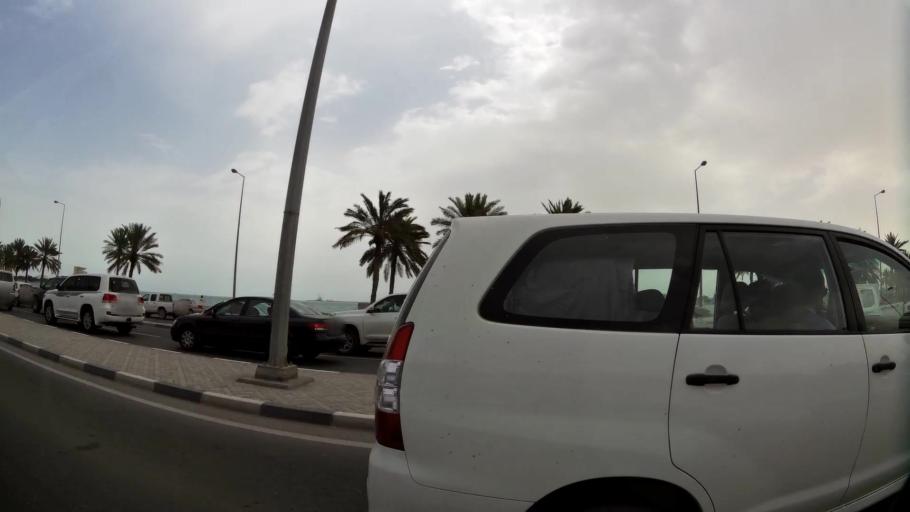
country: QA
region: Baladiyat ad Dawhah
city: Doha
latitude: 25.3100
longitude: 51.5191
